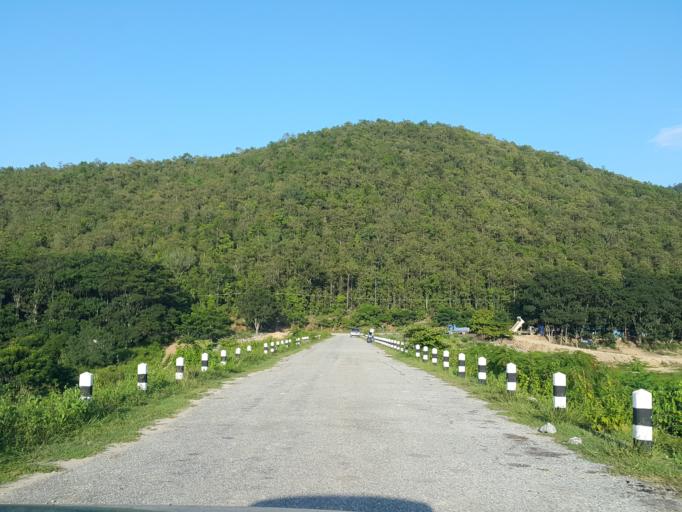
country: TH
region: Chiang Mai
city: Mae On
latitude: 18.7061
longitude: 99.2044
